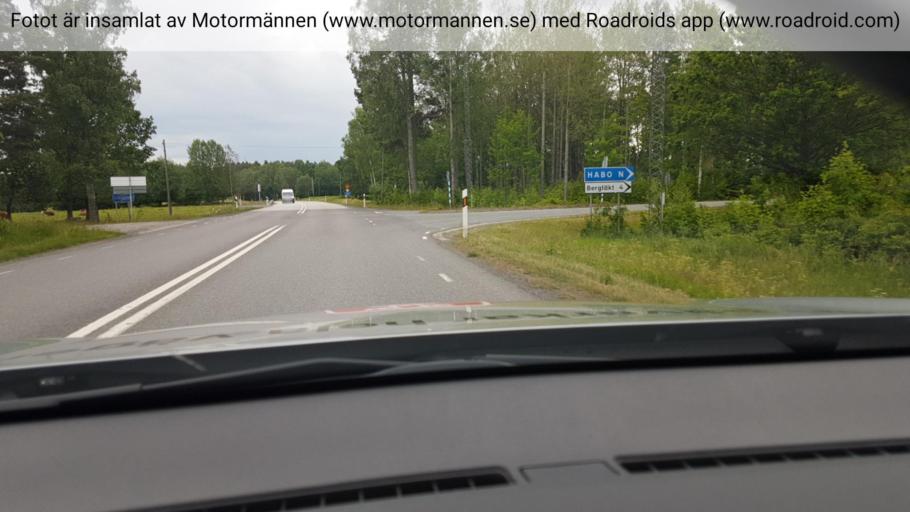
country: SE
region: Joenkoeping
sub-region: Habo Kommun
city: Habo
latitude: 57.9241
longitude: 14.0951
